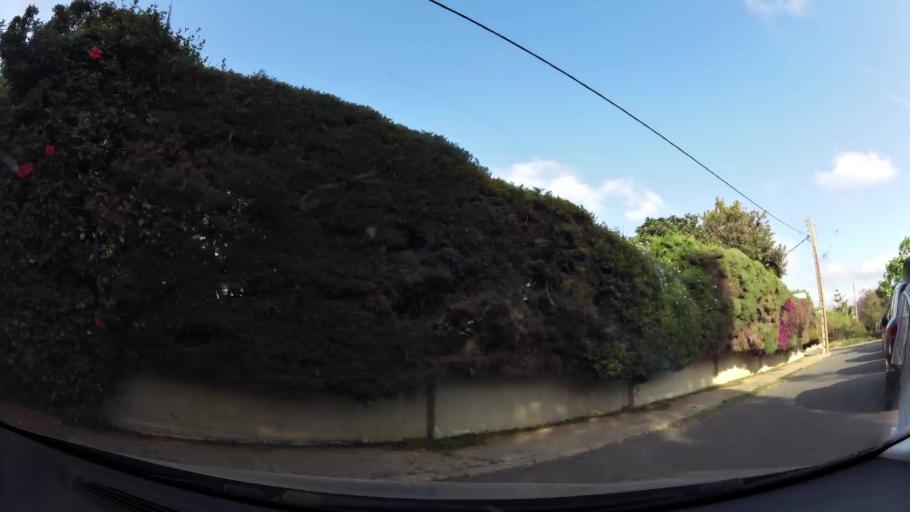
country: MA
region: Rabat-Sale-Zemmour-Zaer
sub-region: Skhirate-Temara
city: Temara
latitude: 33.9581
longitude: -6.8552
